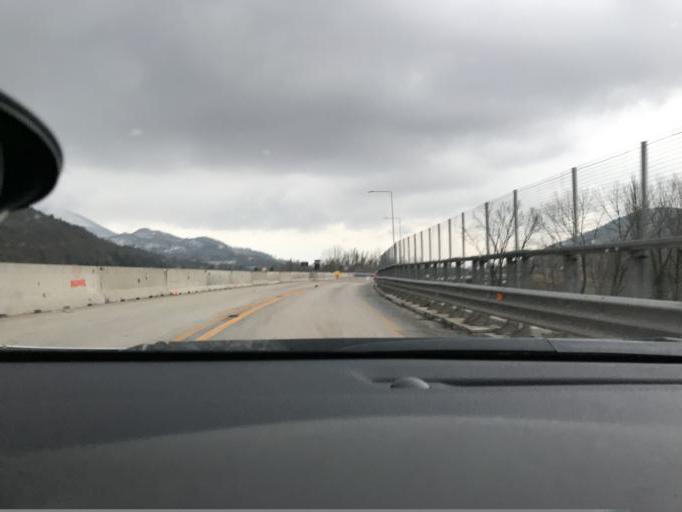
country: IT
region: The Marches
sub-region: Provincia di Ancona
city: Cerreto d'Esi
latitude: 43.3551
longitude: 12.9996
